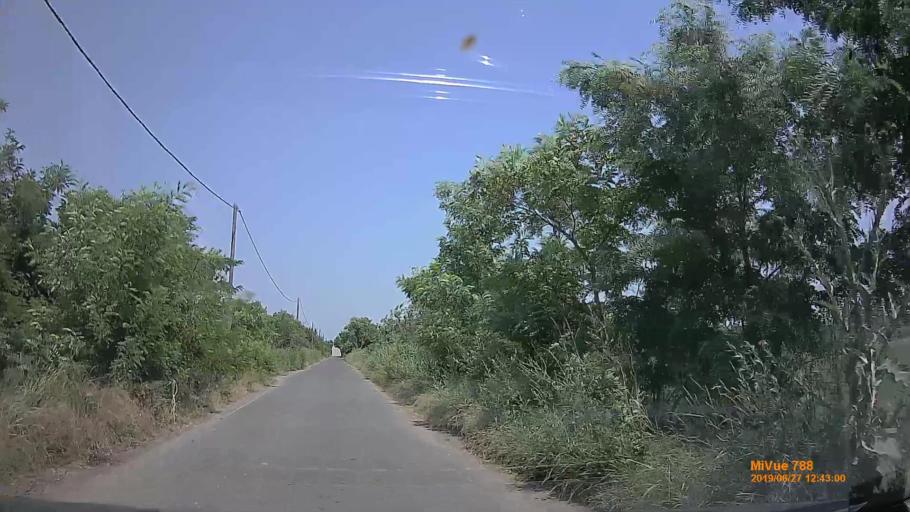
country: HU
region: Pest
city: Tortel
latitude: 47.1863
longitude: 19.8961
